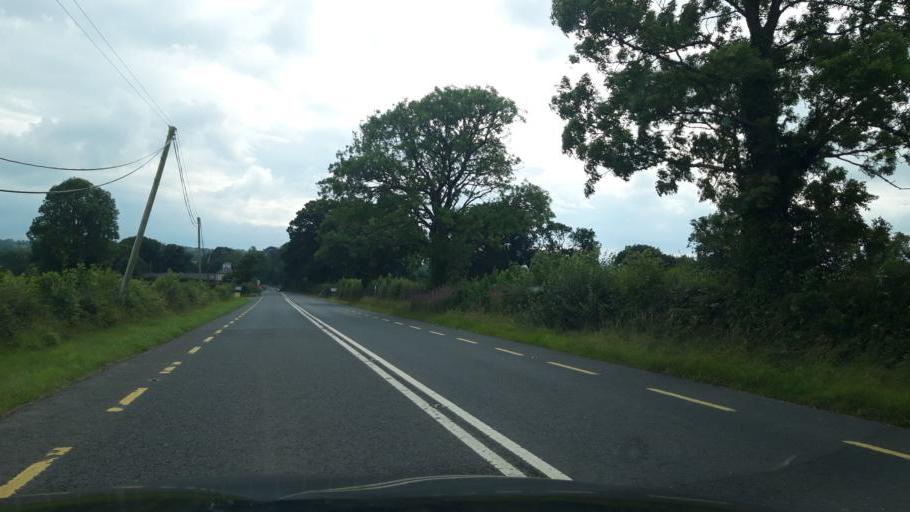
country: IE
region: Leinster
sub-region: Kilkenny
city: Castlecomer
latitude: 52.8484
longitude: -7.1241
